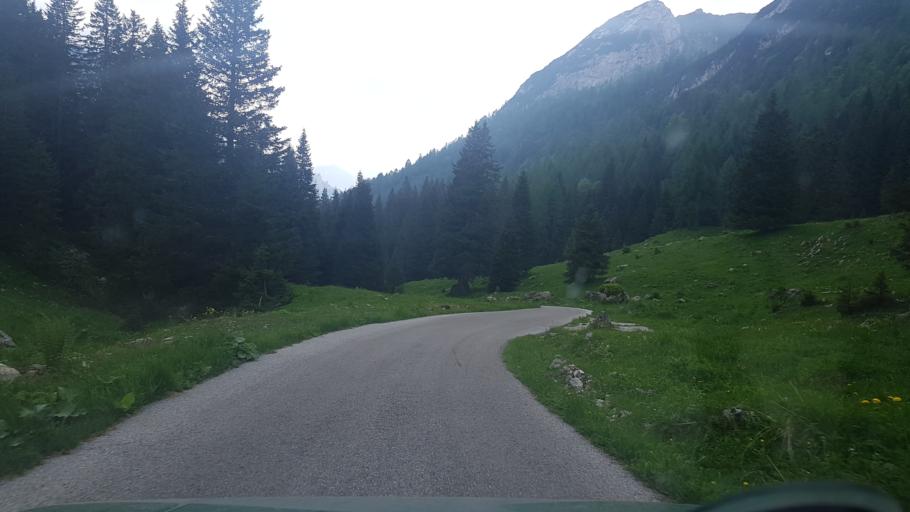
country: IT
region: Friuli Venezia Giulia
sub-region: Provincia di Udine
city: Paularo
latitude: 46.5644
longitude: 13.1731
